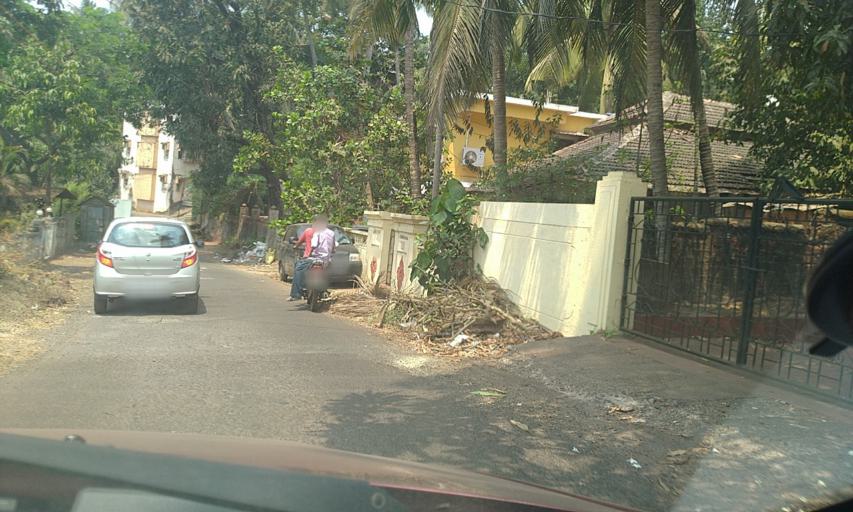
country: IN
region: Goa
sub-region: North Goa
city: Mapuca
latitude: 15.5954
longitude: 73.8103
